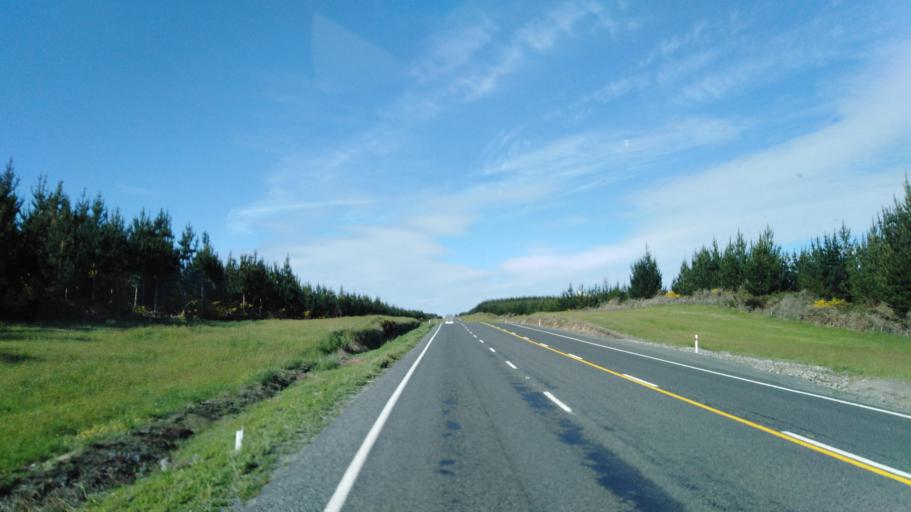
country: NZ
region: Waikato
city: Turangi
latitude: -39.1202
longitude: 175.7997
